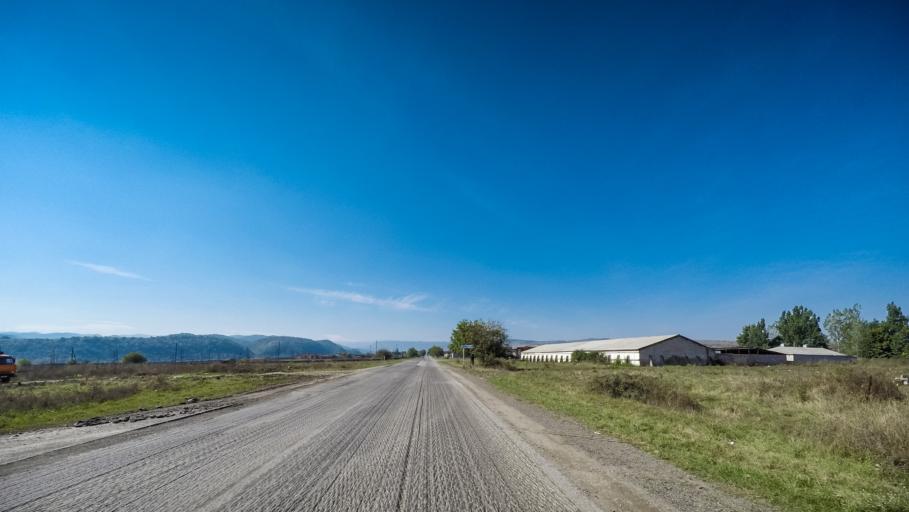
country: RU
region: Kabardino-Balkariya
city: Kamenka
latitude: 43.5673
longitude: 43.4847
